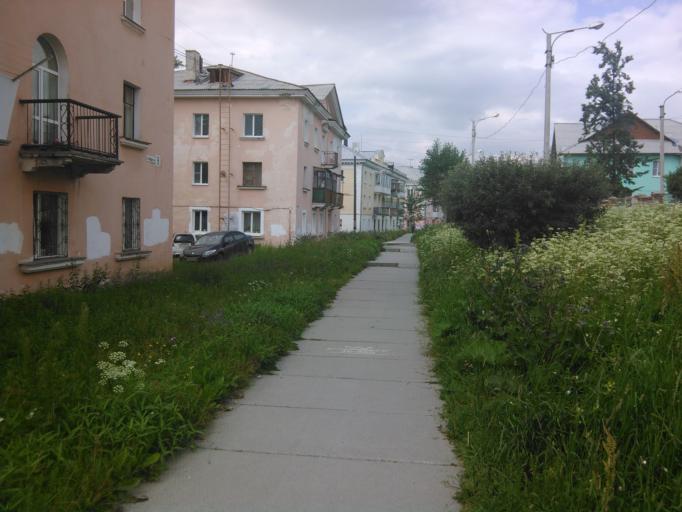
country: RU
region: Sverdlovsk
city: Krasnotur'insk
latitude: 59.7652
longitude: 60.1995
